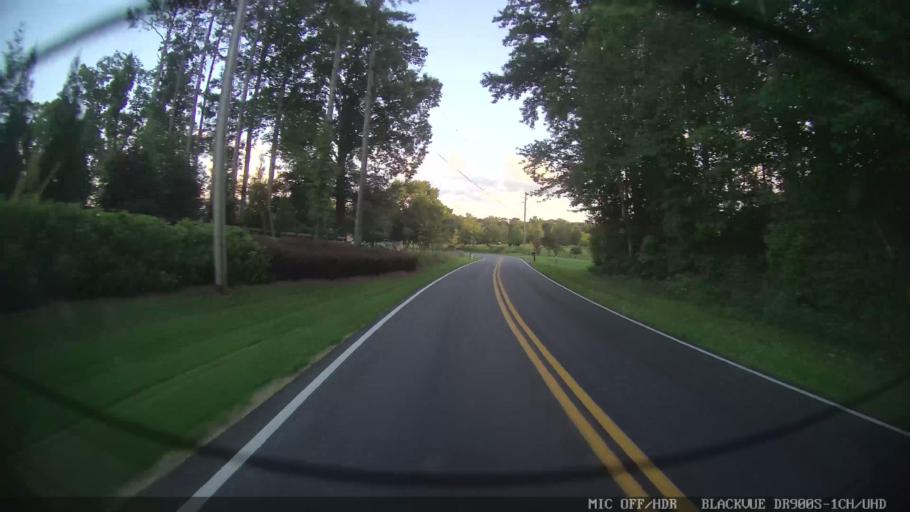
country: US
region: Georgia
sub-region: Forsyth County
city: Cumming
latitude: 34.2262
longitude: -84.2127
